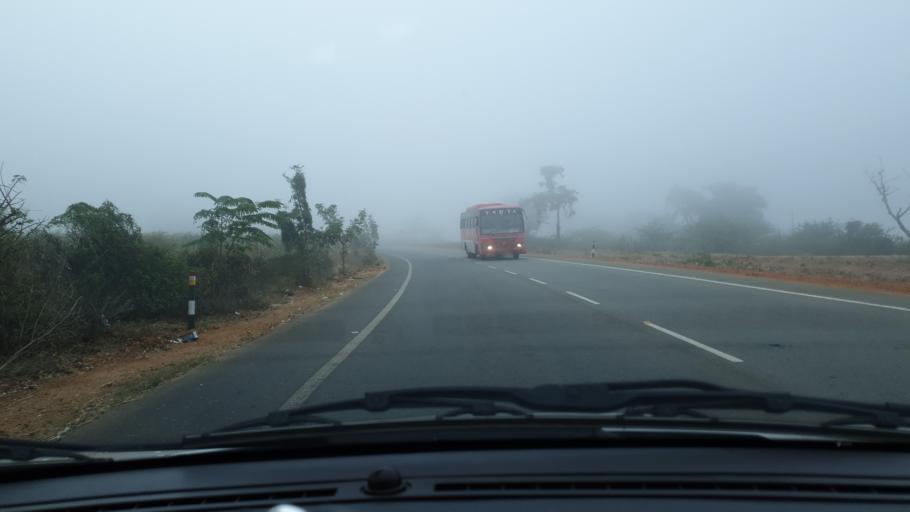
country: IN
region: Telangana
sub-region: Mahbubnagar
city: Nagar Karnul
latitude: 16.6528
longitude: 78.5757
